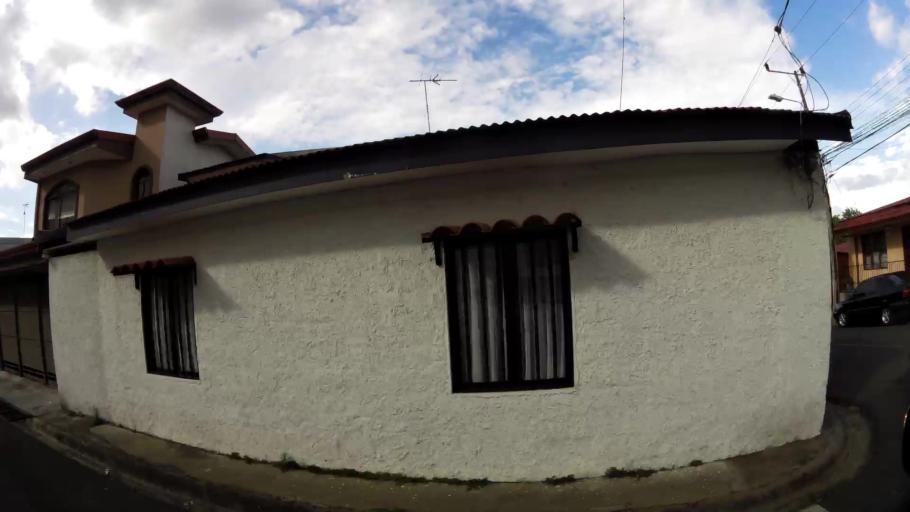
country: CR
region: San Jose
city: Escazu
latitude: 9.9178
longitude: -84.1401
